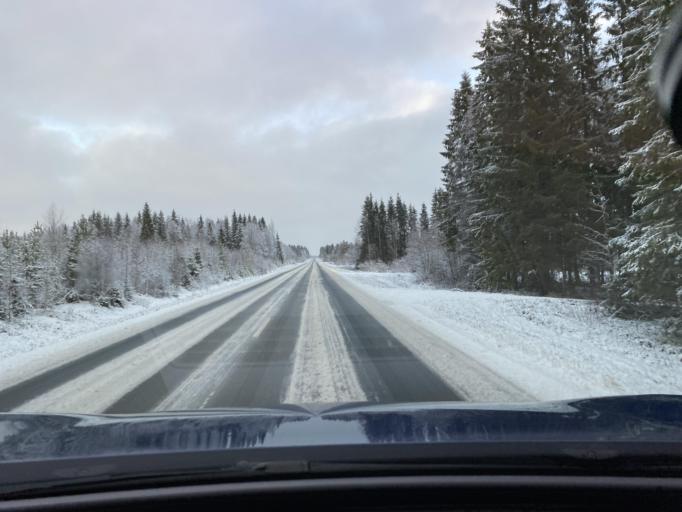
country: FI
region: Lapland
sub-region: Rovaniemi
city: Ranua
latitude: 65.9702
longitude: 26.0987
